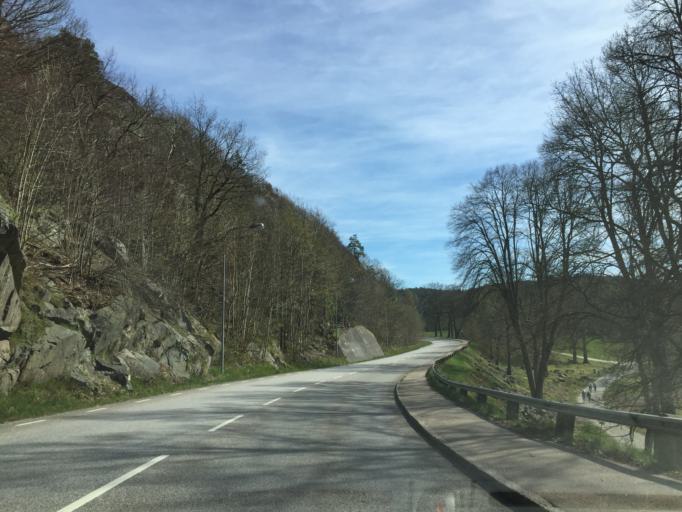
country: SE
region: Vaestra Goetaland
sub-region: Uddevalla Kommun
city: Uddevalla
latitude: 58.3353
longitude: 11.9116
